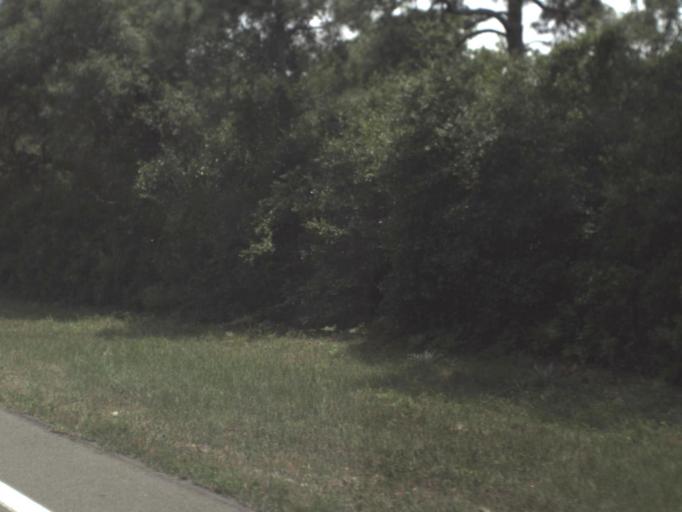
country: US
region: Florida
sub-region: Duval County
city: Atlantic Beach
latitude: 30.4945
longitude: -81.4445
